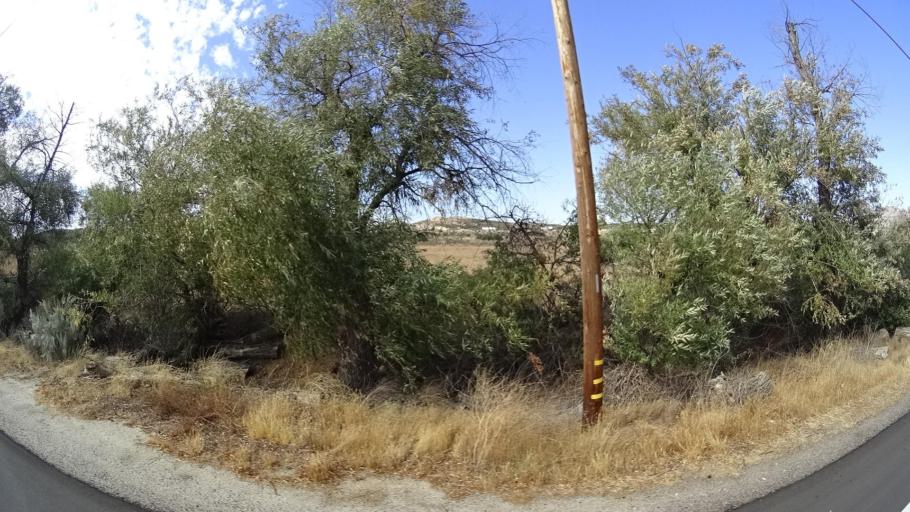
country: MX
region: Baja California
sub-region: Tecate
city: Cereso del Hongo
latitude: 32.6644
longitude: -116.2644
